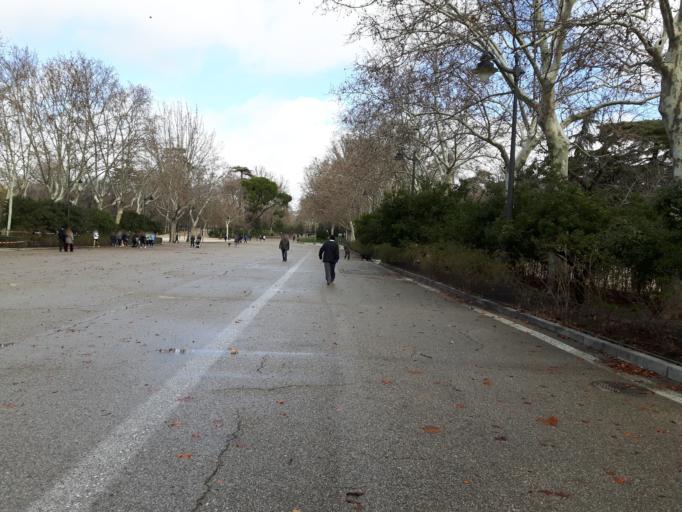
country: ES
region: Madrid
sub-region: Provincia de Madrid
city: Retiro
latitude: 40.4154
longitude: -3.6798
